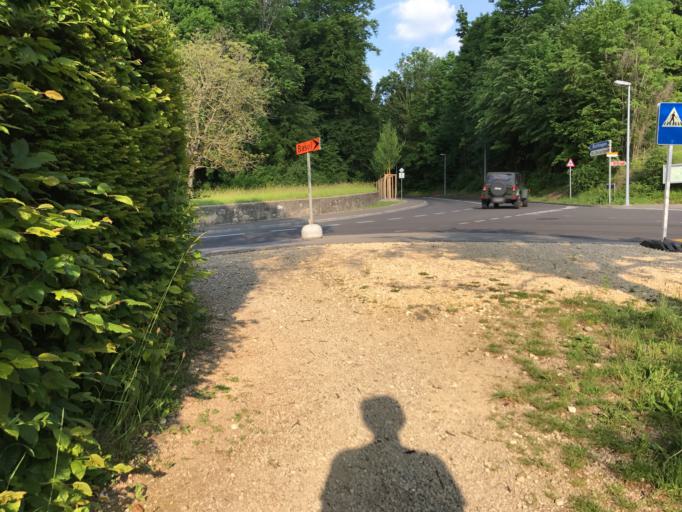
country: CH
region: Basel-City
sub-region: Basel-Stadt
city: Riehen
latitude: 47.5728
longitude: 7.6530
